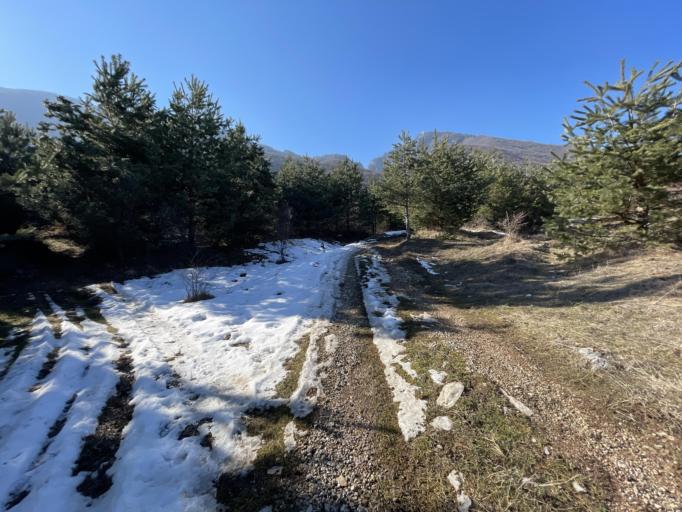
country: XK
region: Gjakova
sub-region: Komuna e Decanit
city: Strellc i Eperm
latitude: 42.6015
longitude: 20.2841
